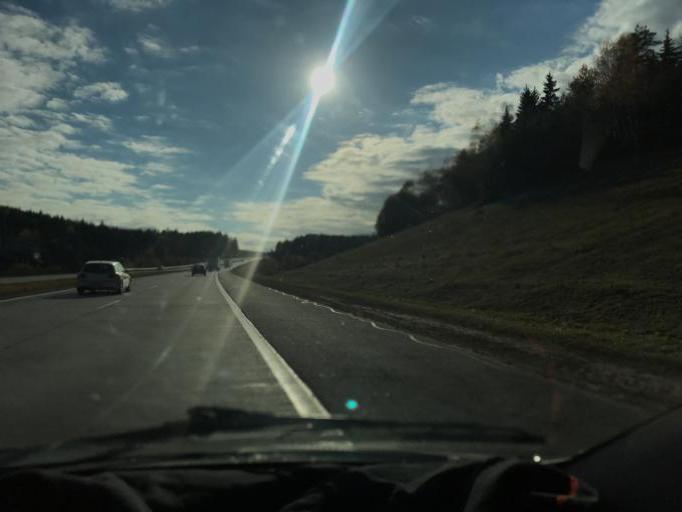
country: BY
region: Minsk
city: Lahoysk
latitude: 54.1101
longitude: 27.8030
